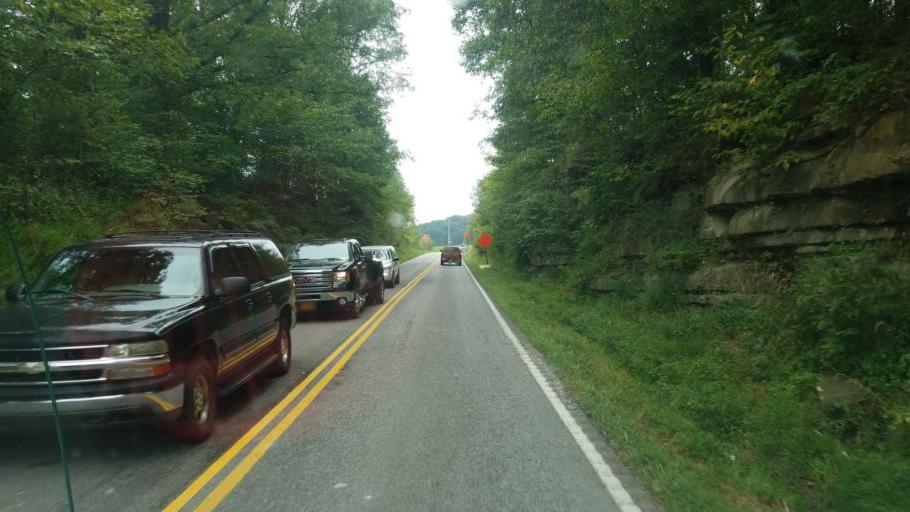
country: US
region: Kentucky
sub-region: Rowan County
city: Morehead
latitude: 38.2136
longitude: -83.4711
